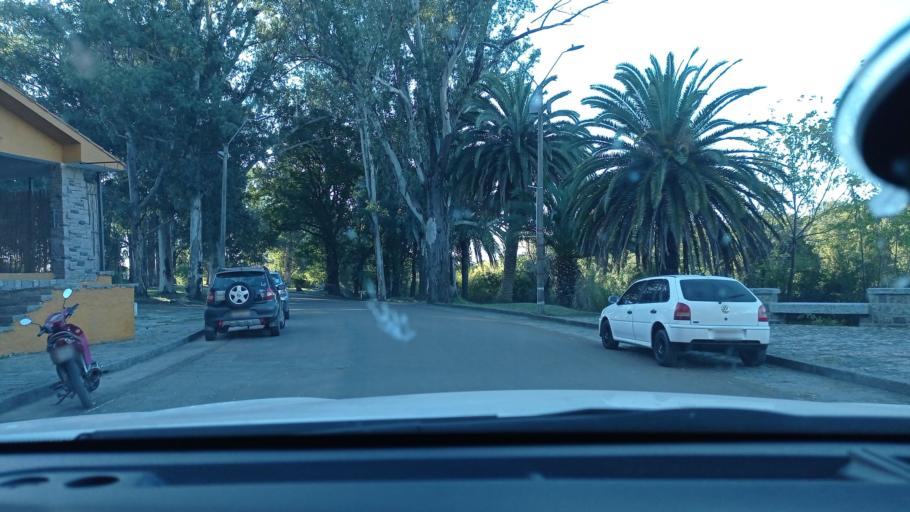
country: UY
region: Florida
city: Florida
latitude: -34.0981
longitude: -56.2042
